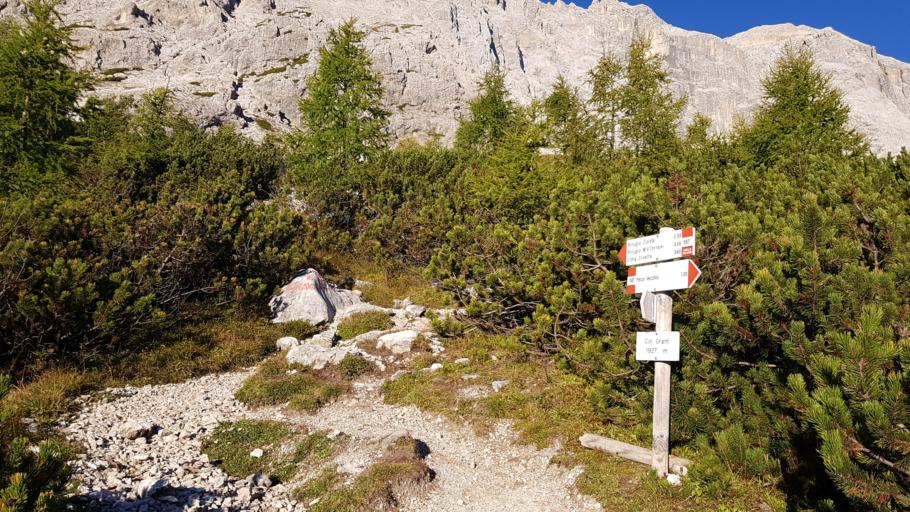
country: IT
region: Veneto
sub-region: Provincia di Belluno
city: Fusine
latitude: 46.3739
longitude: 12.0785
